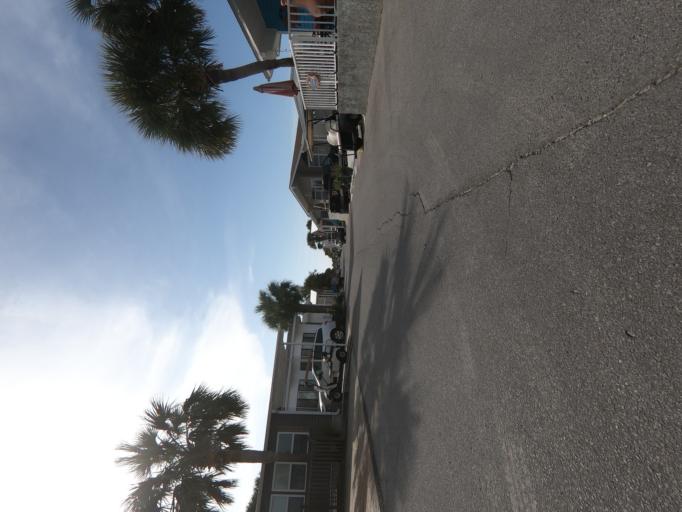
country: US
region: Florida
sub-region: Bay County
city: Lower Grand Lagoon
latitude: 30.1408
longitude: -85.7448
